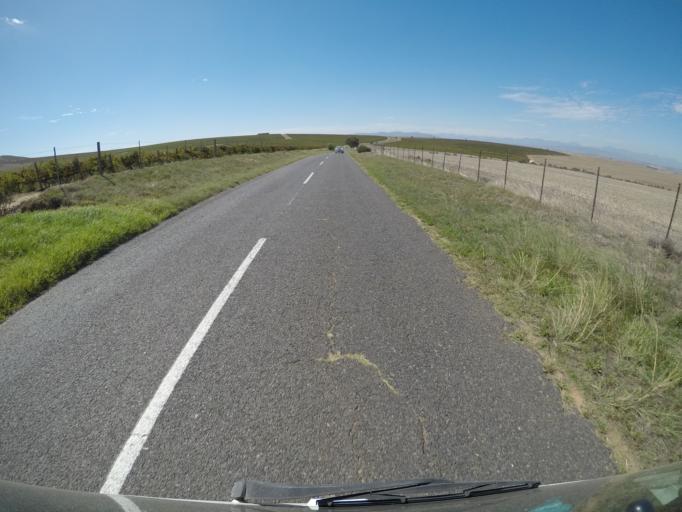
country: ZA
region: Western Cape
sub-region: City of Cape Town
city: Sunset Beach
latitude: -33.7213
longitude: 18.5740
